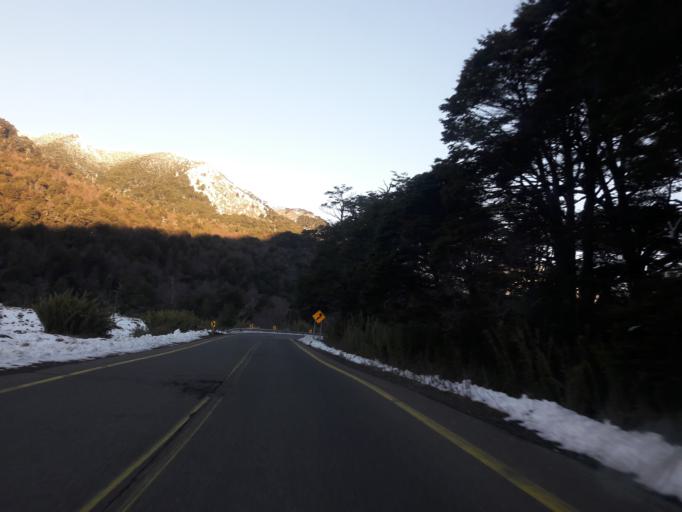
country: CL
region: Araucania
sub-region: Provincia de Cautin
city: Vilcun
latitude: -38.4947
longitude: -71.5217
